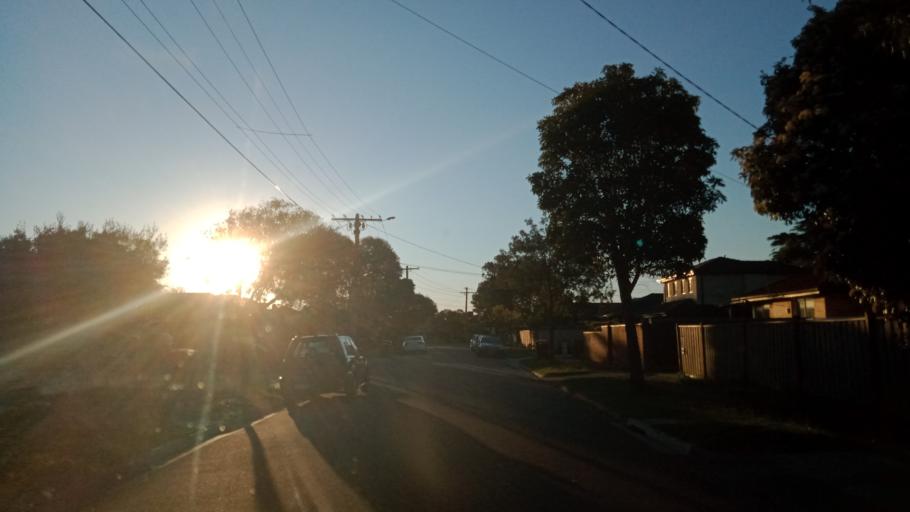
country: AU
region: Victoria
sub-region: Greater Dandenong
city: Springvale
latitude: -37.9358
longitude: 145.1643
